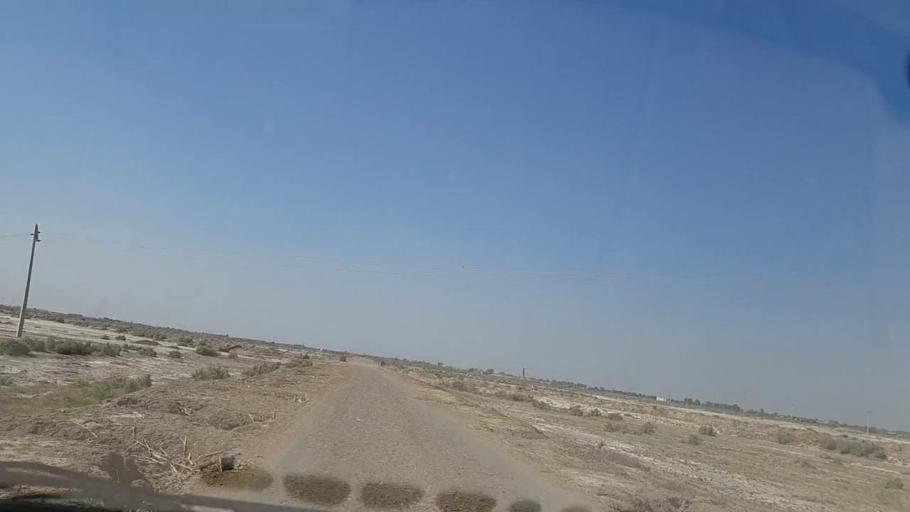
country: PK
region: Sindh
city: Mirwah Gorchani
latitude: 25.3748
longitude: 69.0136
